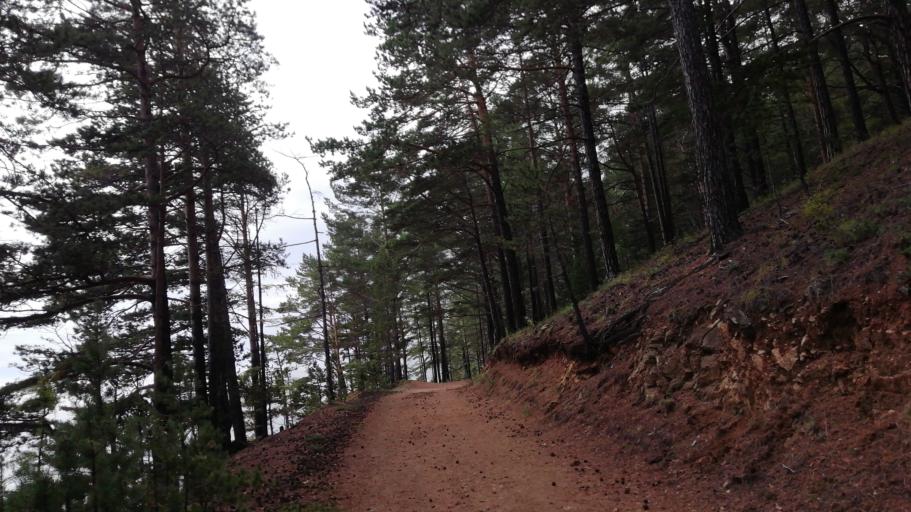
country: RU
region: Irkutsk
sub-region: Irkutskiy Rayon
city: Listvyanka
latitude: 51.8927
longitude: 105.0467
